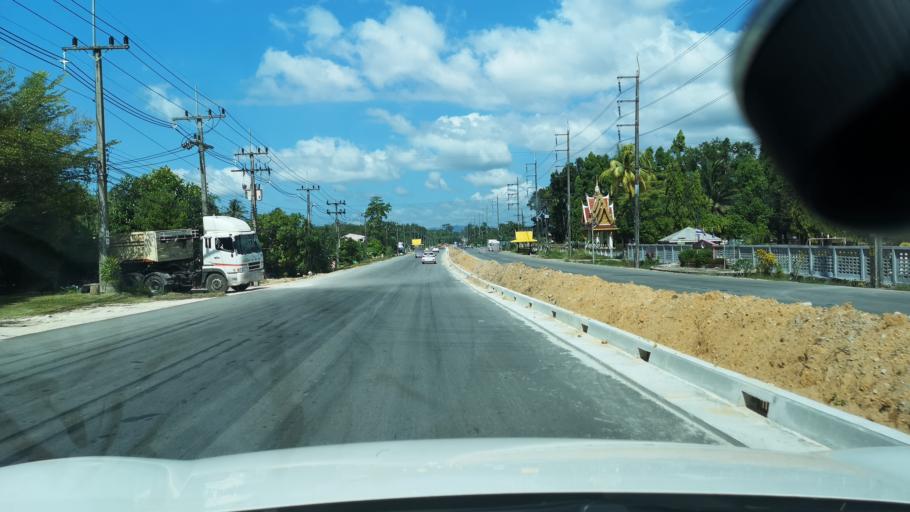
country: TH
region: Phangnga
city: Thai Mueang
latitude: 8.4413
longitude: 98.2569
